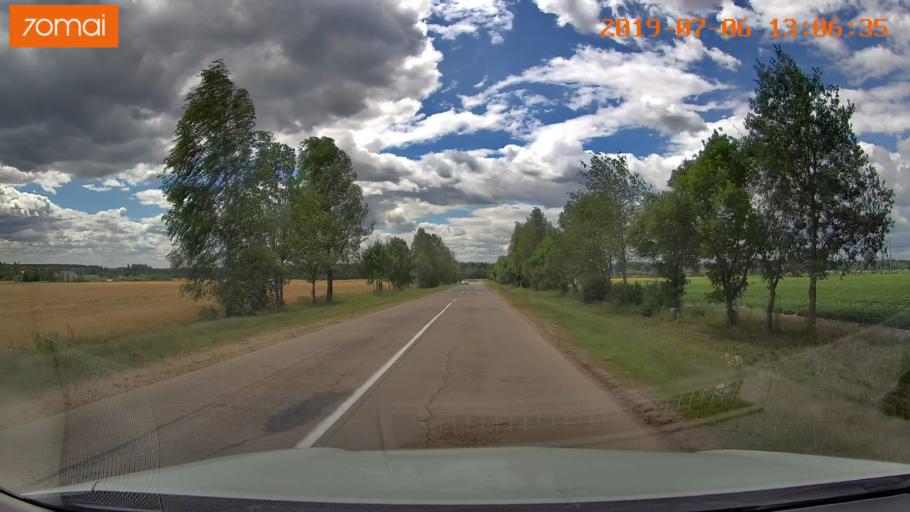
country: BY
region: Minsk
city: Dzyarzhynsk
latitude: 53.6799
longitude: 27.0513
